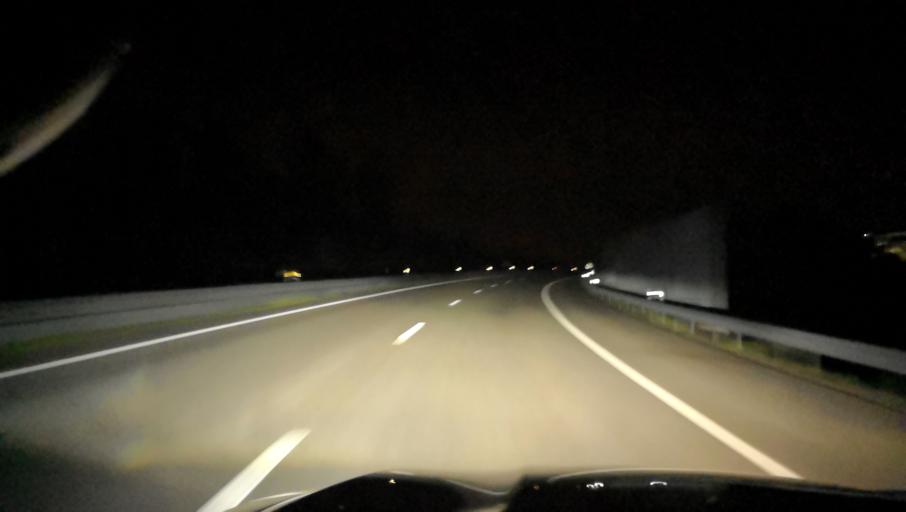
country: PT
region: Viseu
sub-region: Oliveira de Frades
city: Oliveira de Frades
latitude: 40.6814
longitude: -8.1812
